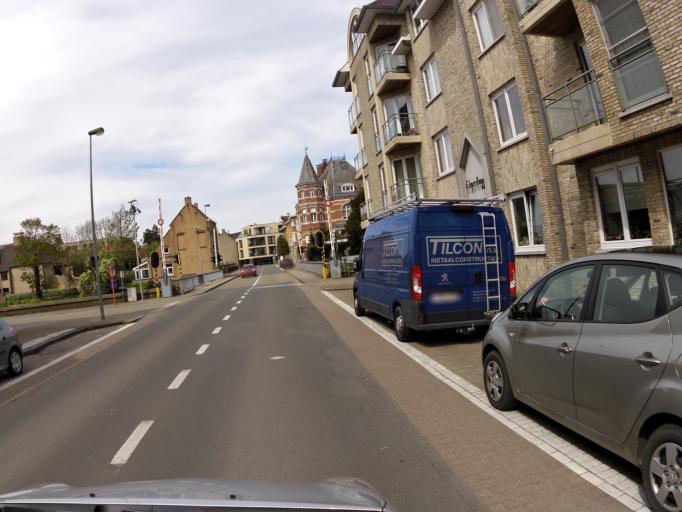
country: BE
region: Flanders
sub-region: Provincie West-Vlaanderen
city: Veurne
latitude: 51.0678
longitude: 2.6646
